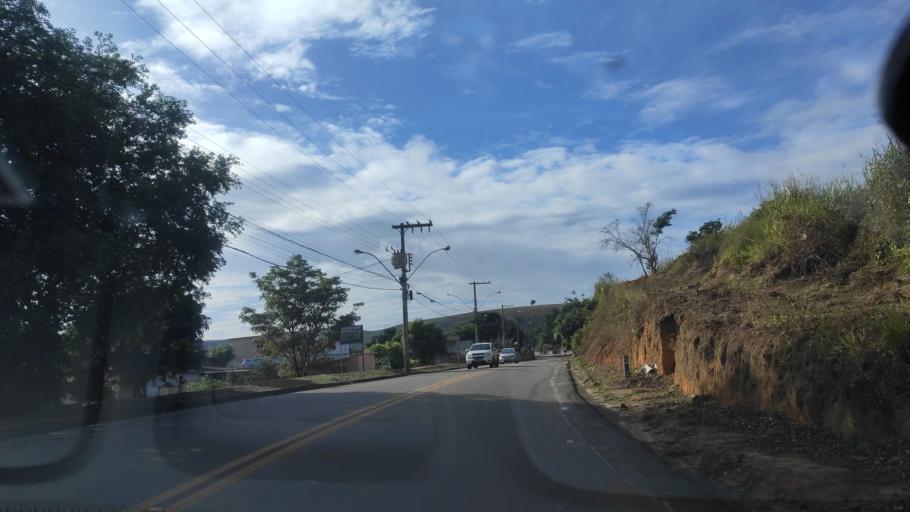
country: BR
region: Espirito Santo
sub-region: Nova Venecia
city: Nova Venecia
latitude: -18.7117
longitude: -40.3837
